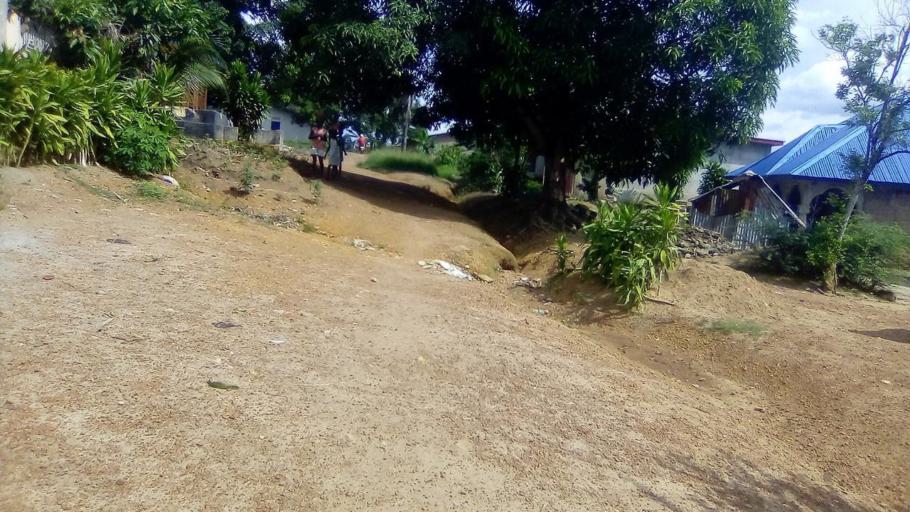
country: SL
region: Southern Province
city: Bo
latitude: 7.9571
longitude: -11.7178
